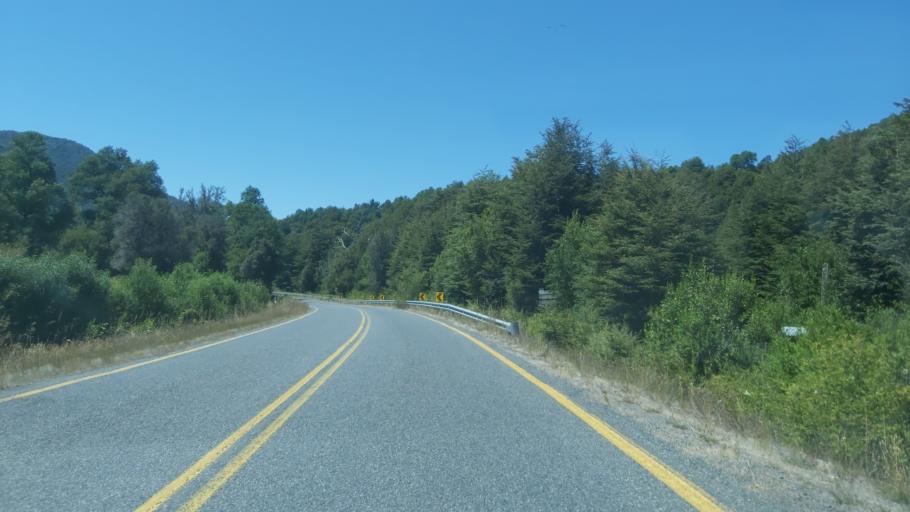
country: CL
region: Araucania
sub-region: Provincia de Cautin
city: Vilcun
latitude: -38.4624
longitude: -71.7219
